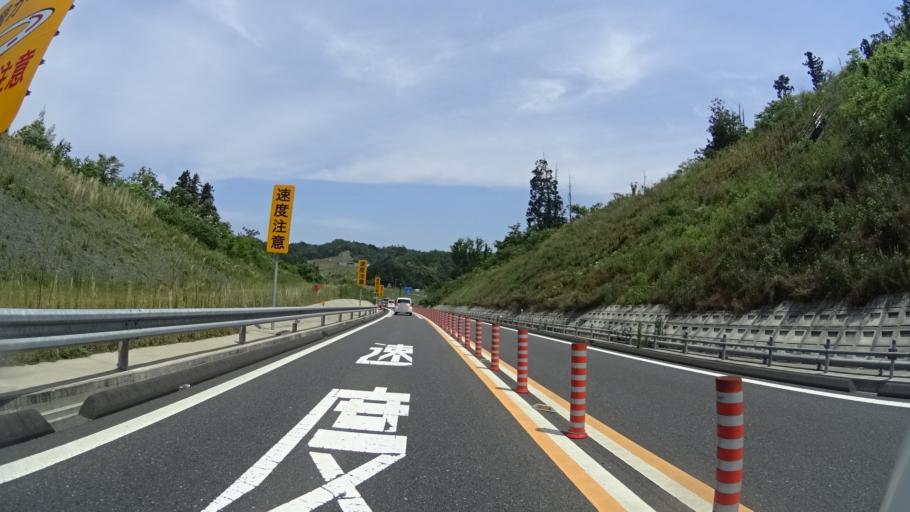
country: JP
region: Kyoto
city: Miyazu
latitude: 35.5733
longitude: 135.1216
